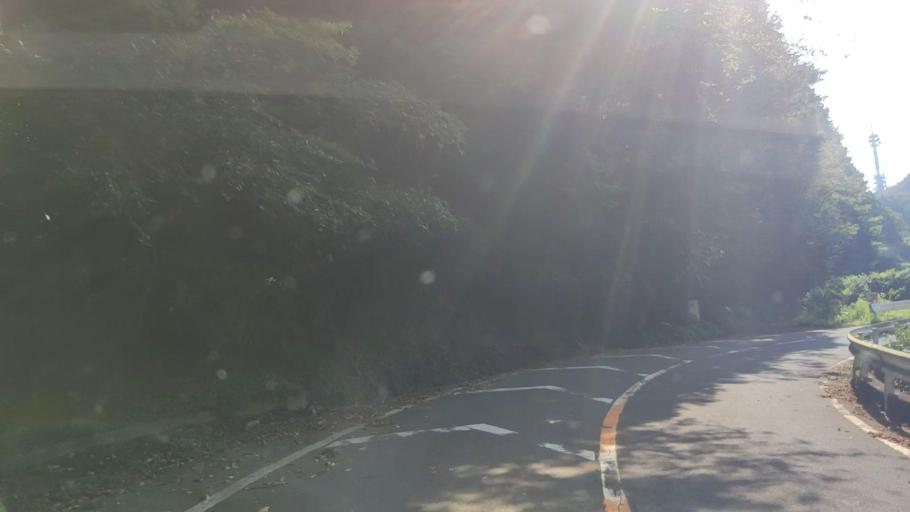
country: JP
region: Shizuoka
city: Shizuoka-shi
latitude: 34.9777
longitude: 138.4721
